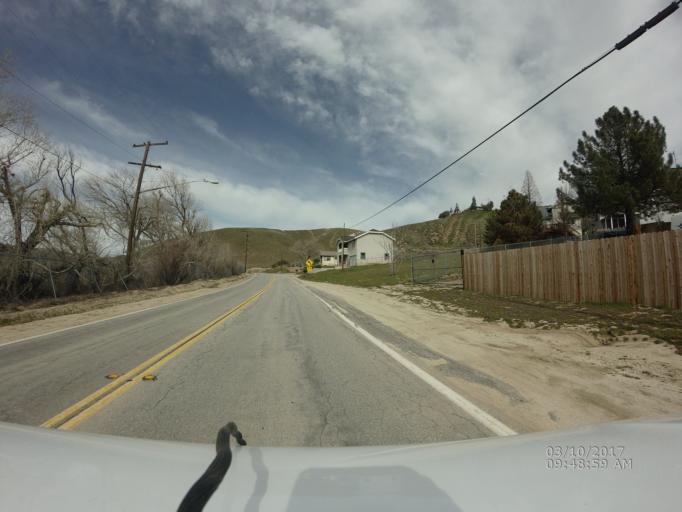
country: US
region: California
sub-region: Los Angeles County
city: Green Valley
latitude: 34.6677
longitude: -118.3931
